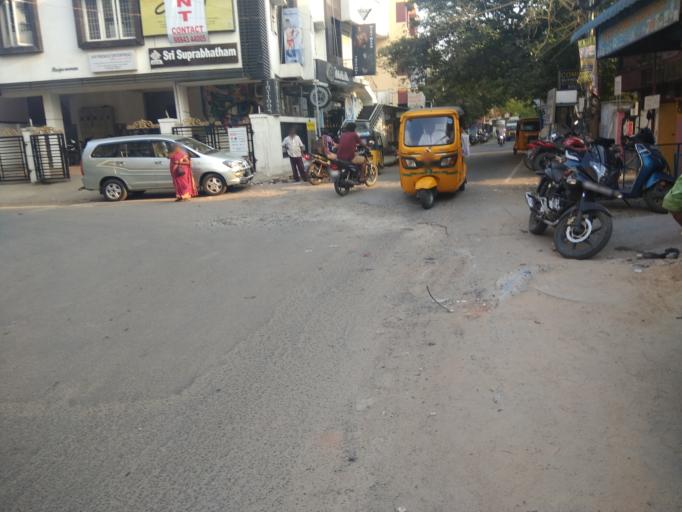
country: IN
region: Tamil Nadu
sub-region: Chennai
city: Chetput
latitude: 13.0584
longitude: 80.2222
